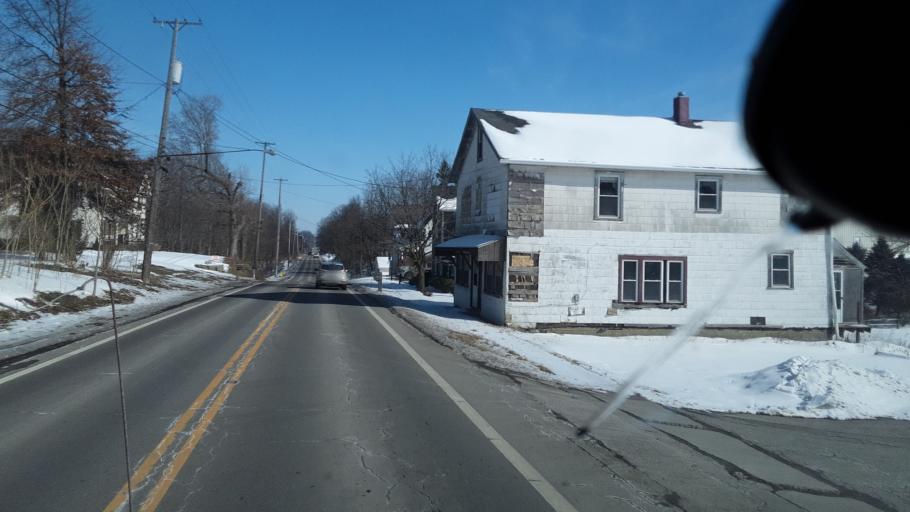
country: US
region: Ohio
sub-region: Columbiana County
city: Leetonia
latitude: 40.9440
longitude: -80.7905
